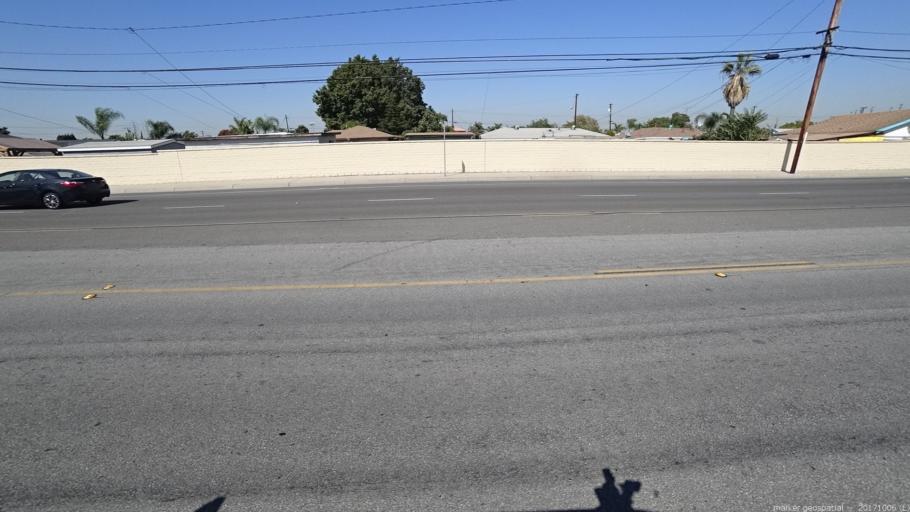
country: US
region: California
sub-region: Orange County
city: Stanton
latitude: 33.7883
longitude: -117.9958
